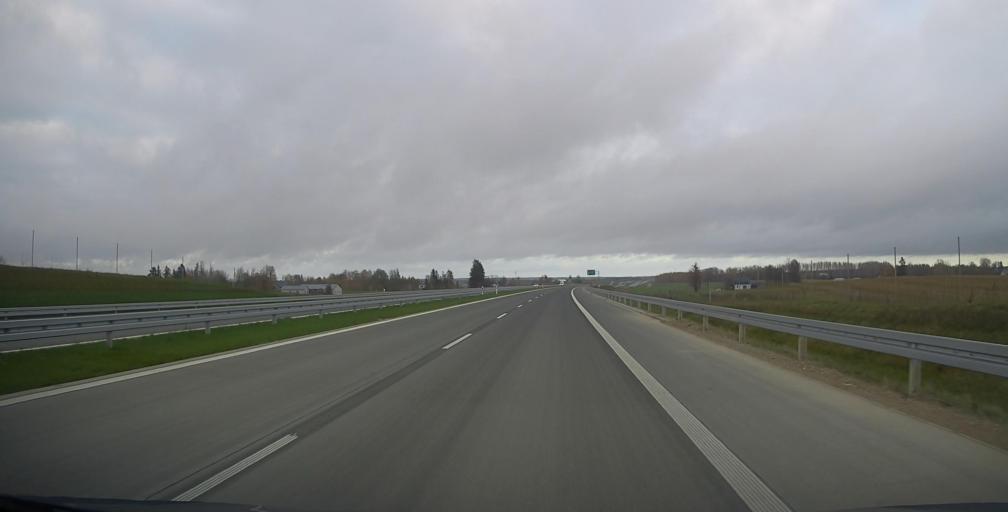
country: PL
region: Podlasie
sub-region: Powiat suwalski
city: Raczki
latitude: 53.9585
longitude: 22.7721
